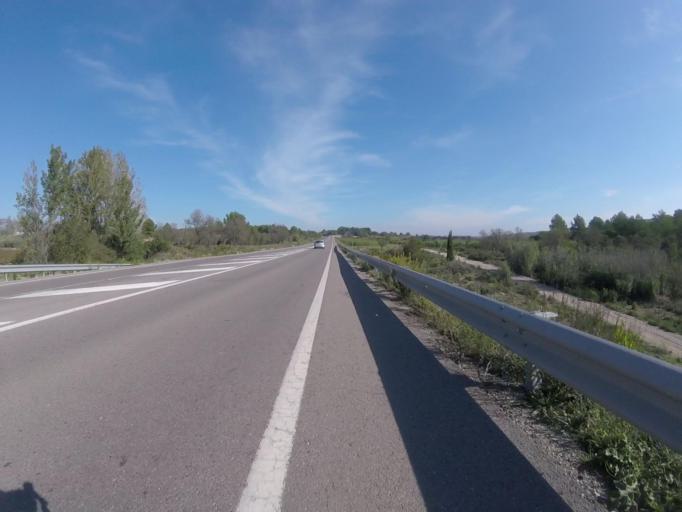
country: ES
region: Valencia
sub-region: Provincia de Castello
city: Benlloch
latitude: 40.2540
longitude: 0.0753
